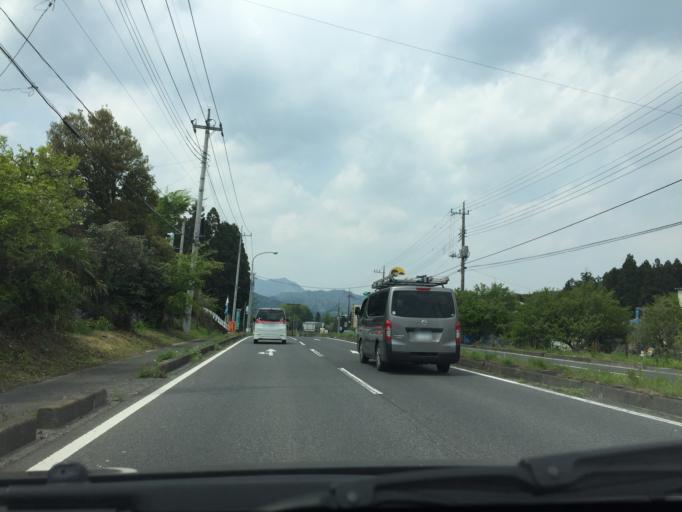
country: JP
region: Tochigi
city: Imaichi
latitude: 36.7687
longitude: 139.7152
